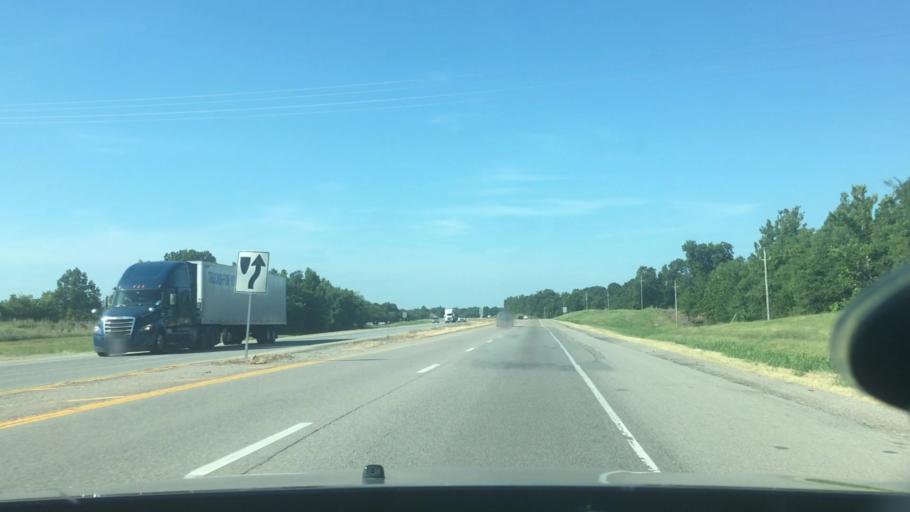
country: US
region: Oklahoma
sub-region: Atoka County
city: Atoka
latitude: 34.3130
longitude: -96.1723
